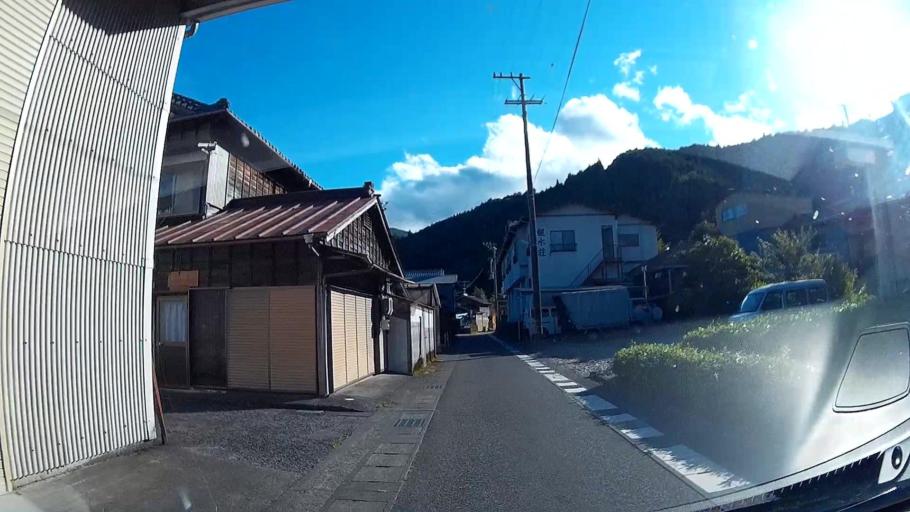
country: JP
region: Shizuoka
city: Shizuoka-shi
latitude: 35.2208
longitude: 138.2403
